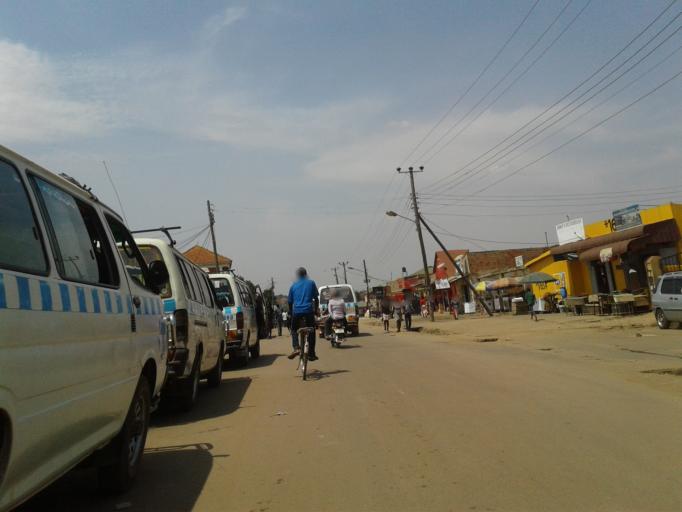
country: UG
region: Central Region
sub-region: Kampala District
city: Kampala
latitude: 0.2559
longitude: 32.6352
